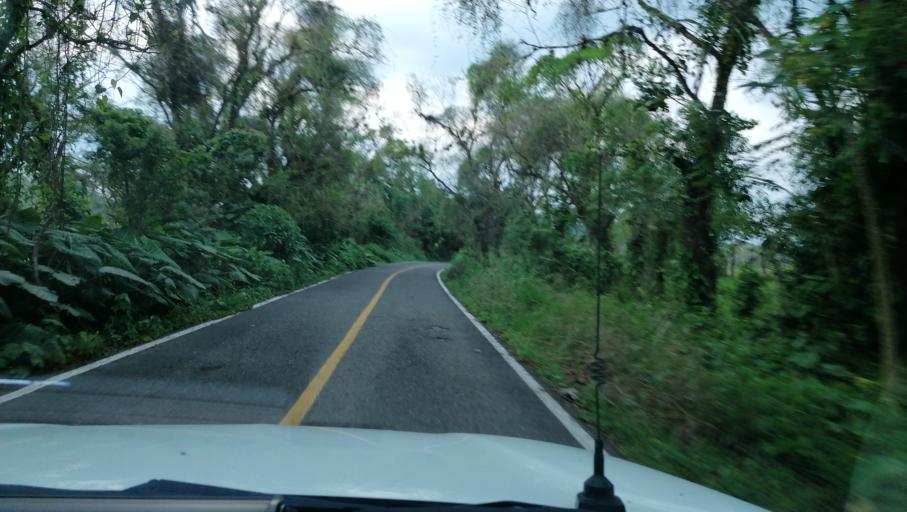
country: MX
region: Chiapas
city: Pichucalco
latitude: 17.5150
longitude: -93.1551
